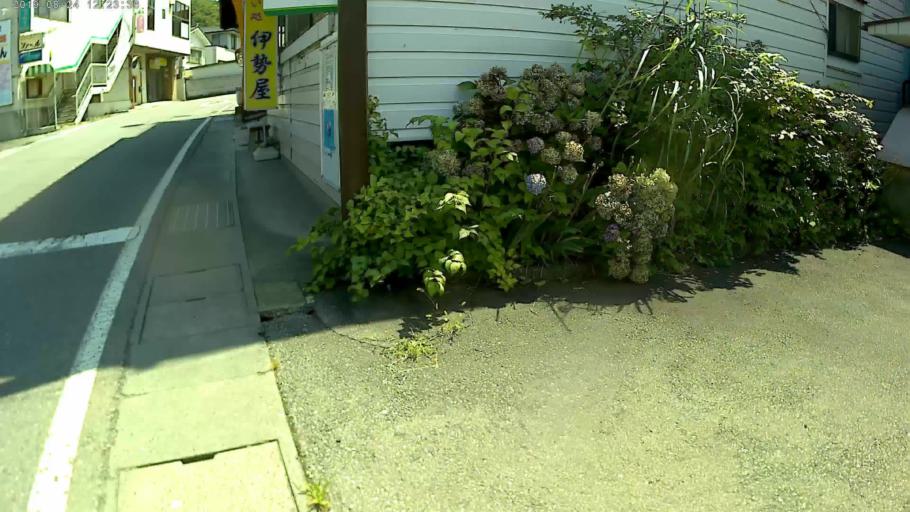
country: JP
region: Nagano
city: Komoro
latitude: 36.2649
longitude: 138.3634
